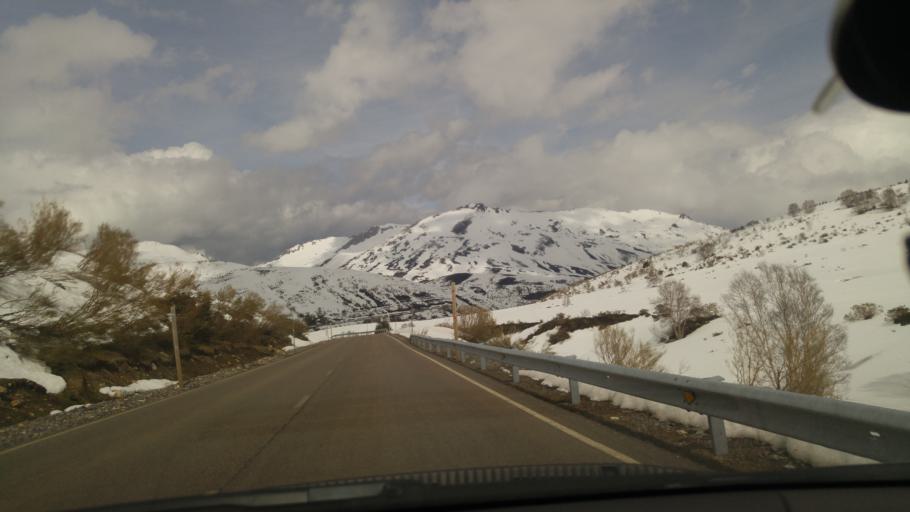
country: ES
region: Castille and Leon
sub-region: Provincia de Leon
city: Puebla de Lillo
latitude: 43.0574
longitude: -5.3755
